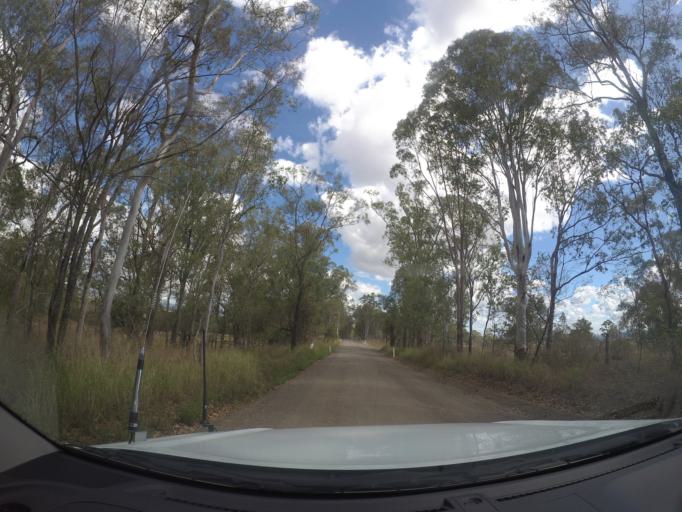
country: AU
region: Queensland
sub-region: Logan
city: Cedar Vale
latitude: -27.9013
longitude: 152.9867
